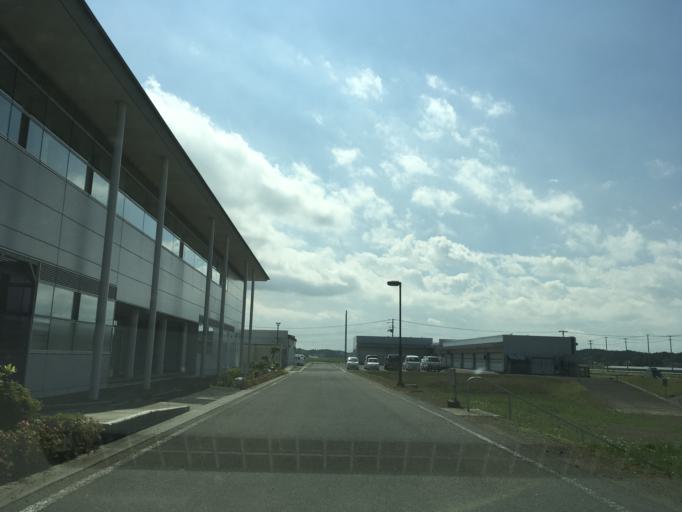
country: JP
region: Miyagi
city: Wakuya
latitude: 38.6649
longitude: 141.1598
